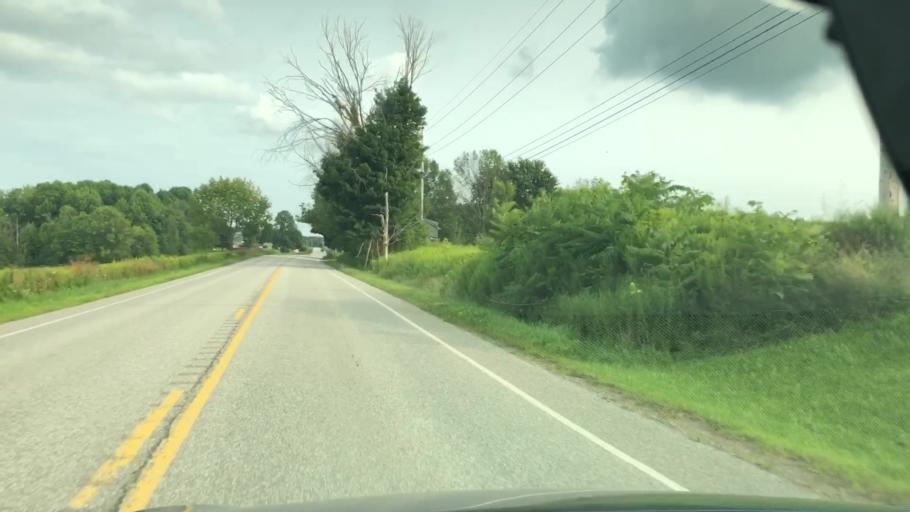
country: US
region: Pennsylvania
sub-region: Erie County
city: Union City
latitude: 41.9535
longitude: -79.8514
